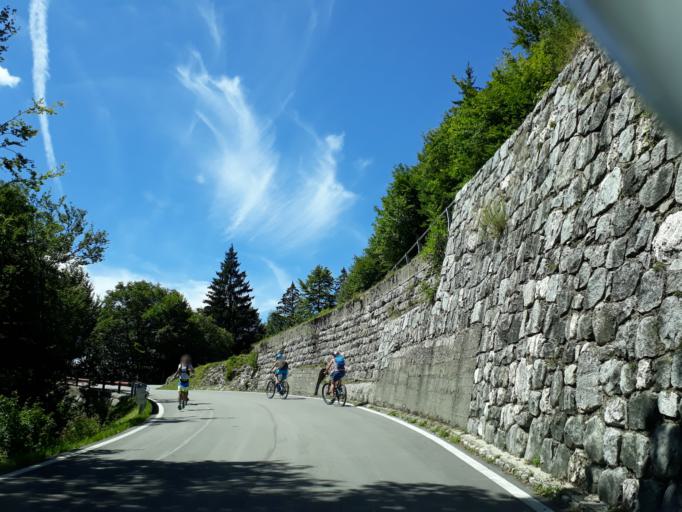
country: IT
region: Trentino-Alto Adige
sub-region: Provincia di Trento
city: Pieve di Ledro
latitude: 45.8511
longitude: 10.6662
